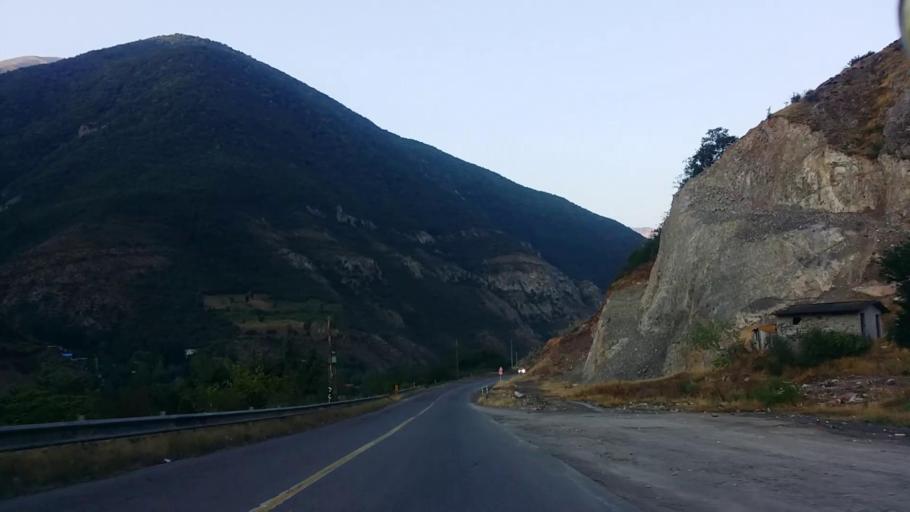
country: IR
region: Mazandaran
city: Chalus
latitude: 36.3871
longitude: 51.2767
